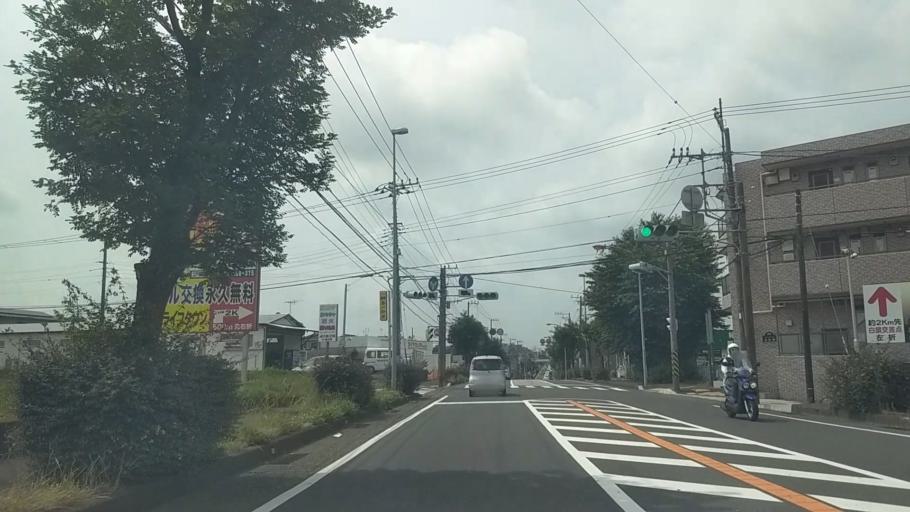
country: JP
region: Kanagawa
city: Fujisawa
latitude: 35.3714
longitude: 139.4788
